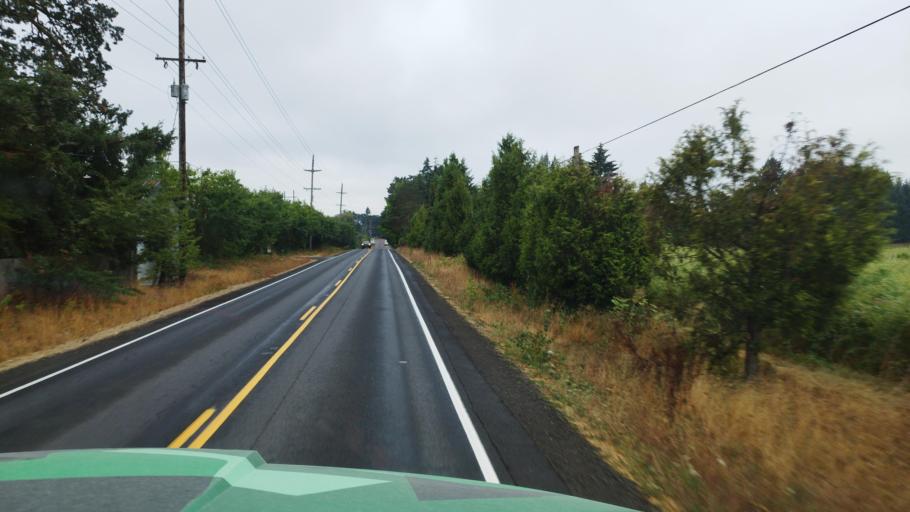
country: US
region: Oregon
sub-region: Washington County
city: Cornelius
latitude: 45.5302
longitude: -123.0816
